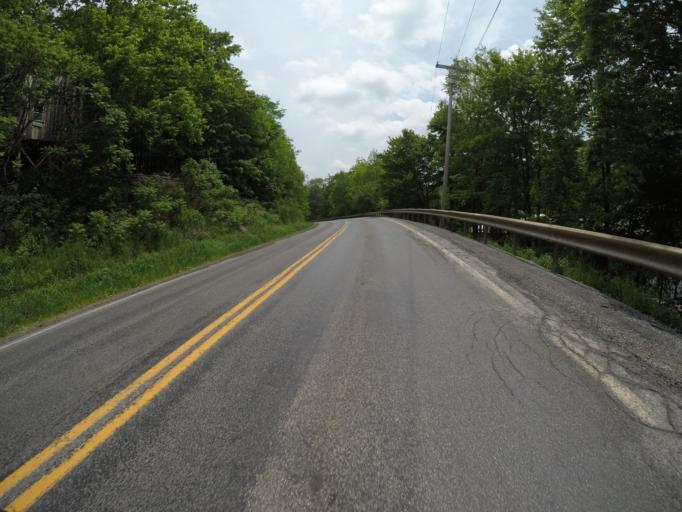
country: US
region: New York
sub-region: Delaware County
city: Delhi
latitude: 42.2596
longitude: -74.7757
